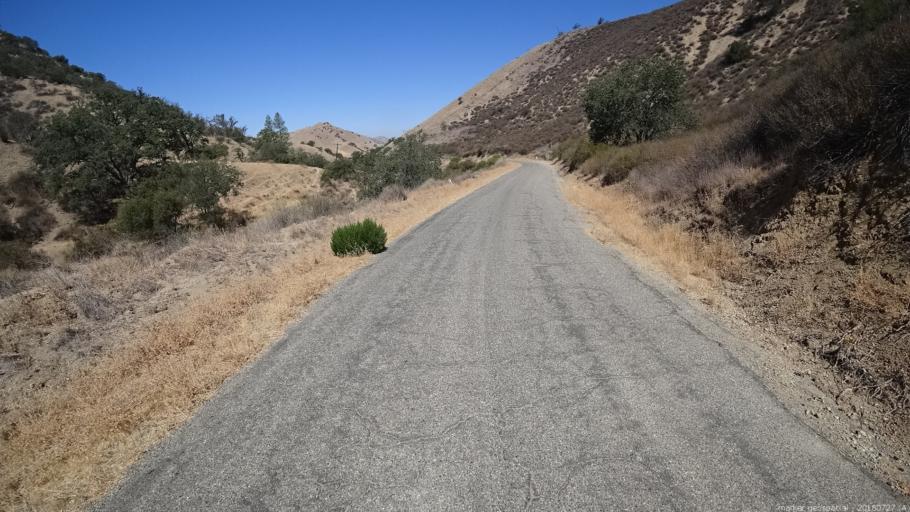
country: US
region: California
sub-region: Monterey County
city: King City
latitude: 36.2966
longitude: -120.9004
